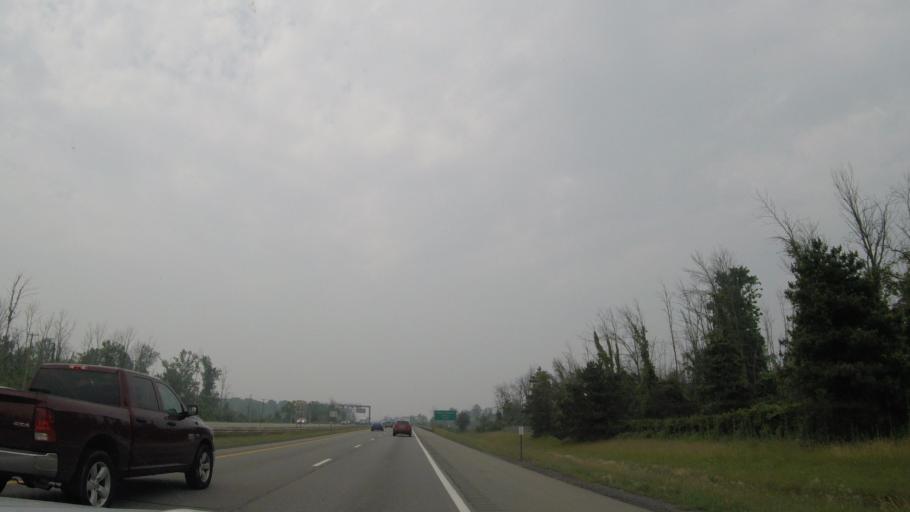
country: US
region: New York
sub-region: Erie County
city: Grandyle Village
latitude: 43.0563
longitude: -78.9904
